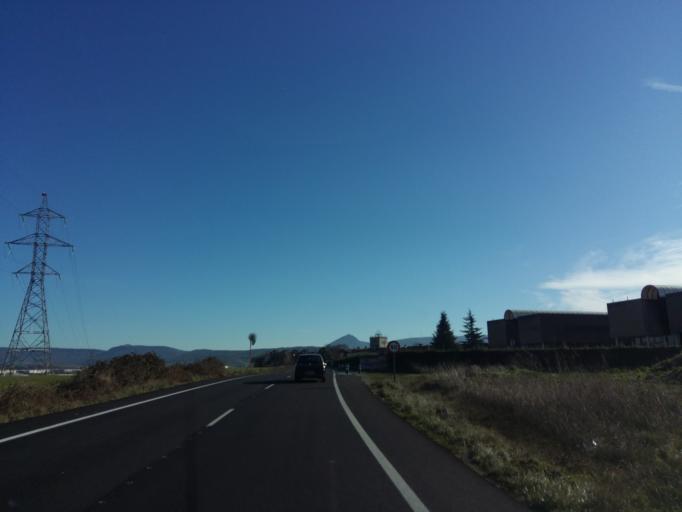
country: ES
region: Navarre
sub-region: Provincia de Navarra
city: Iturrama
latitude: 42.7910
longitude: -1.6484
